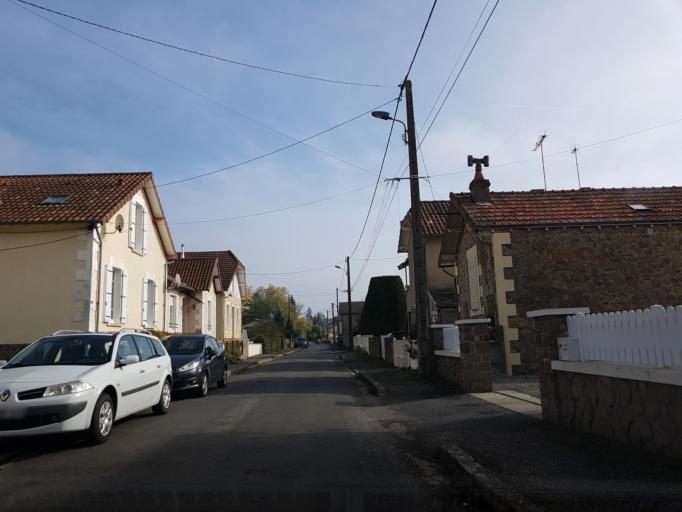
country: FR
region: Poitou-Charentes
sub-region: Departement de la Charente
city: Chabanais
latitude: 45.8747
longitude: 0.7141
